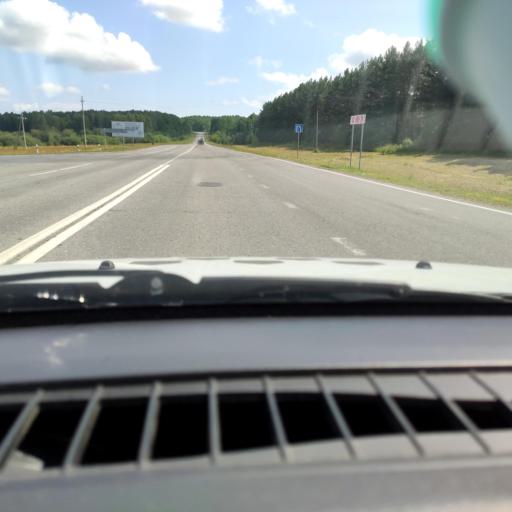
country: RU
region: Bashkortostan
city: Verkhniye Kigi
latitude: 55.3900
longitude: 58.6577
